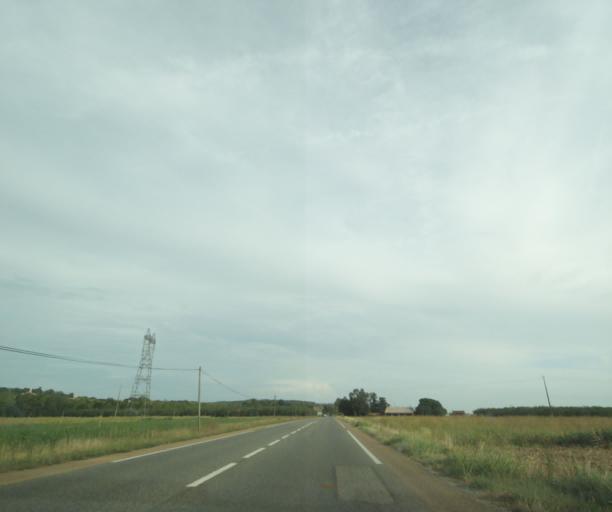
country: FR
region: Midi-Pyrenees
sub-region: Departement du Tarn-et-Garonne
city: Grisolles
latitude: 43.8534
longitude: 1.2798
